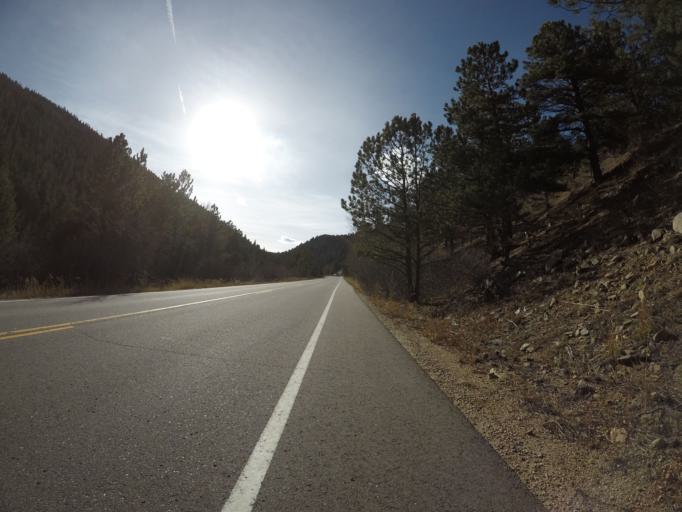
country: US
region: Colorado
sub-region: Boulder County
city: Nederland
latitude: 40.0626
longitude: -105.4837
